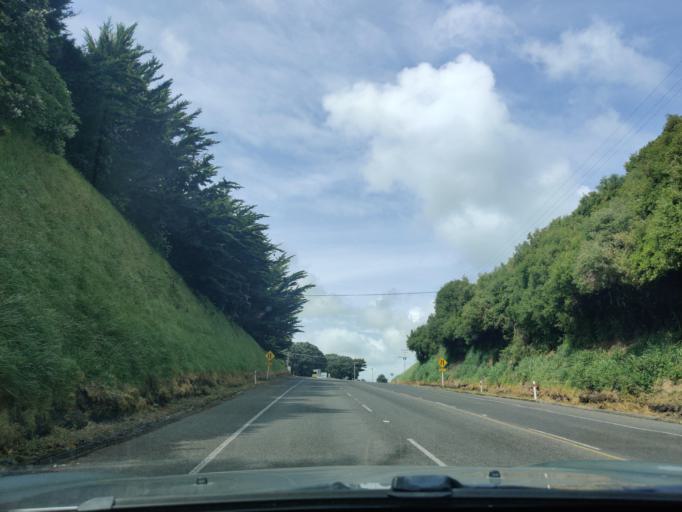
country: NZ
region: Taranaki
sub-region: South Taranaki District
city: Hawera
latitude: -39.5773
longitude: 174.2163
